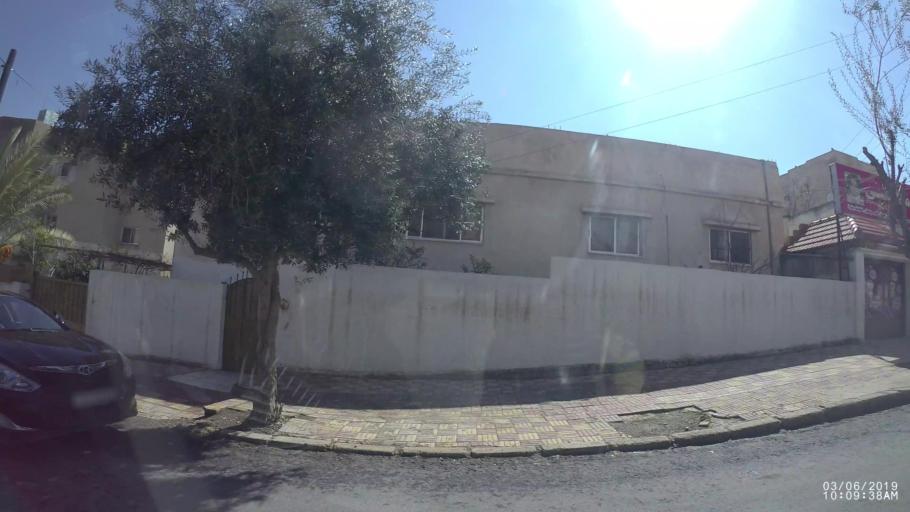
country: JO
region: Amman
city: Amman
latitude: 31.9849
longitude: 35.9833
